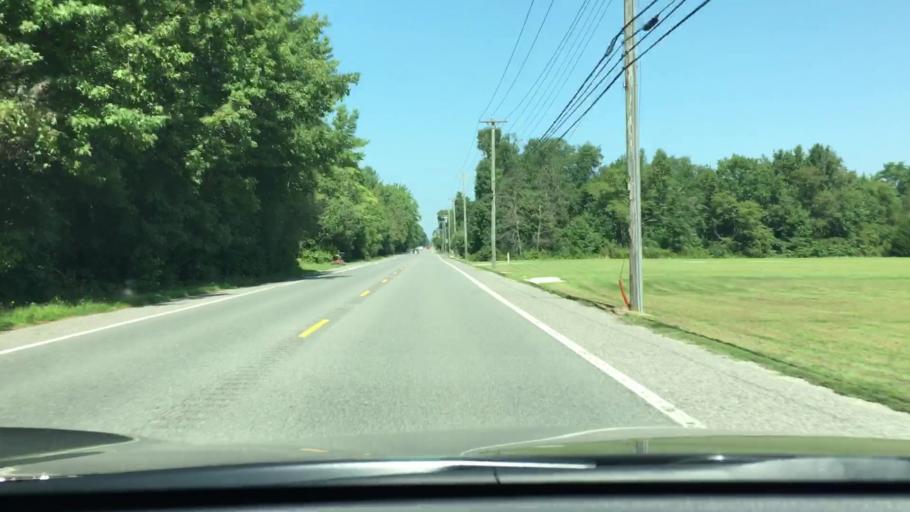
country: US
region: New Jersey
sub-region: Cumberland County
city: Laurel Lake
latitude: 39.3002
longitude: -75.0016
